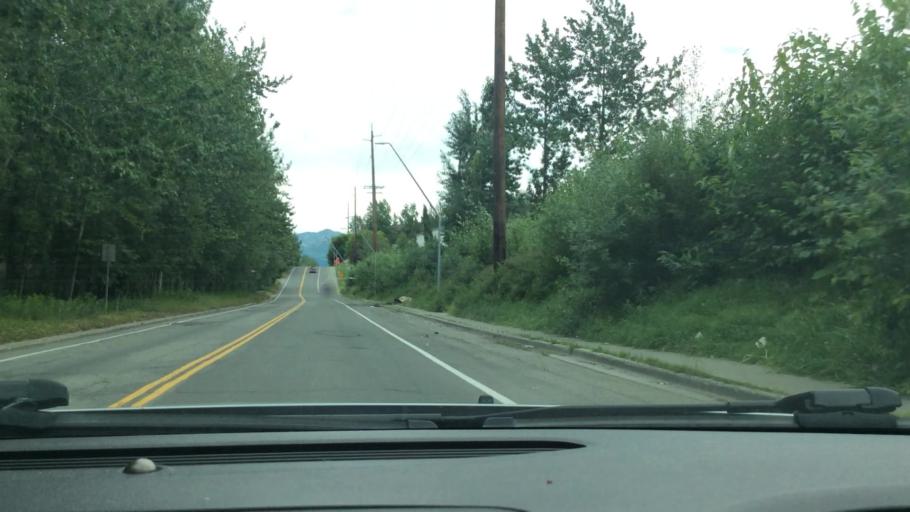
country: US
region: Alaska
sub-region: Anchorage Municipality
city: Elmendorf Air Force Base
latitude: 61.2242
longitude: -149.7424
